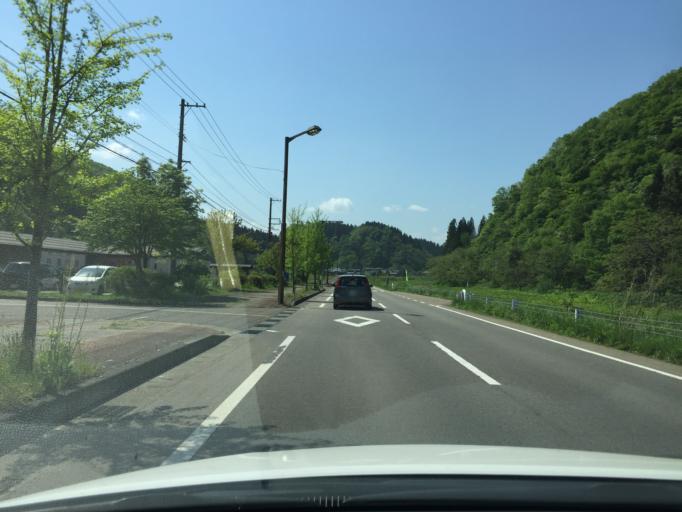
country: JP
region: Niigata
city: Kamo
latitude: 37.6239
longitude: 139.1040
